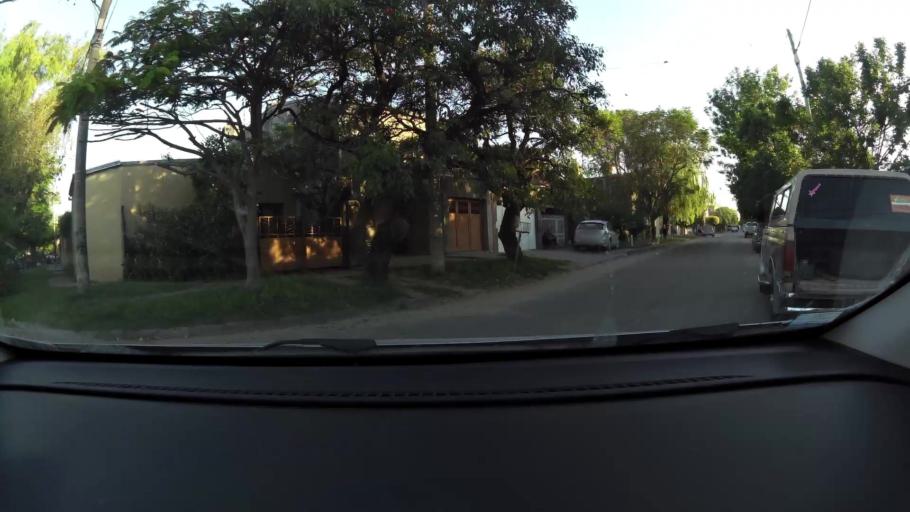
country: AR
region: Santa Fe
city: Santa Fe de la Vera Cruz
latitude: -31.5981
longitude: -60.6885
